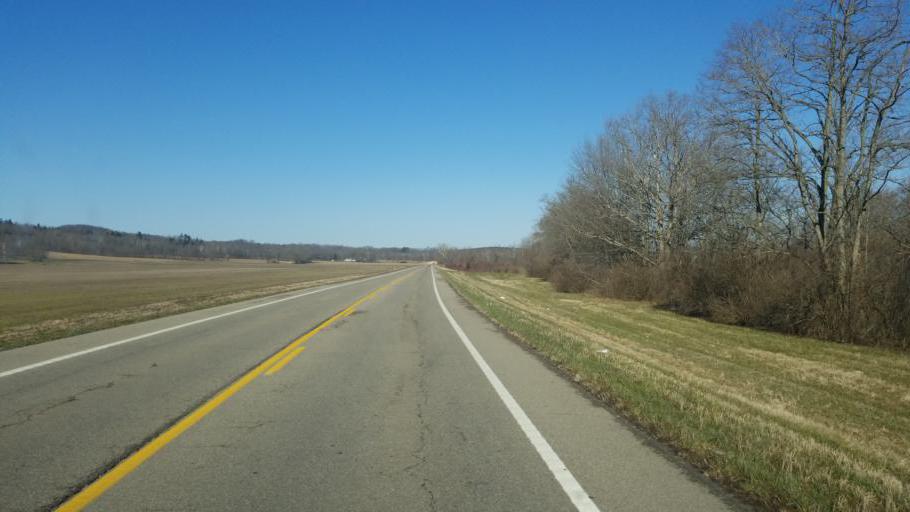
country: US
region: Ohio
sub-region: Highland County
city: Greenfield
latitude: 39.2211
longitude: -83.2980
